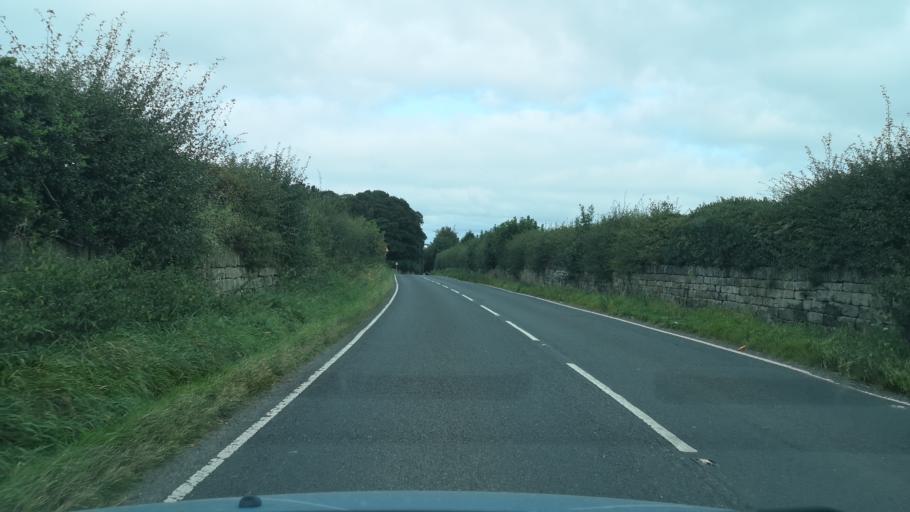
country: GB
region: England
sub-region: City and Borough of Wakefield
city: Walton
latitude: 53.6449
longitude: -1.4797
